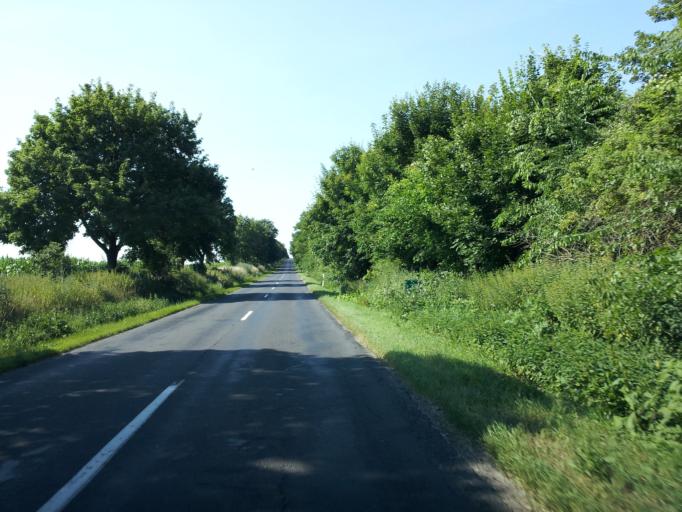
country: HU
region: Fejer
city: Lovasbereny
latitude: 47.3538
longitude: 18.5805
